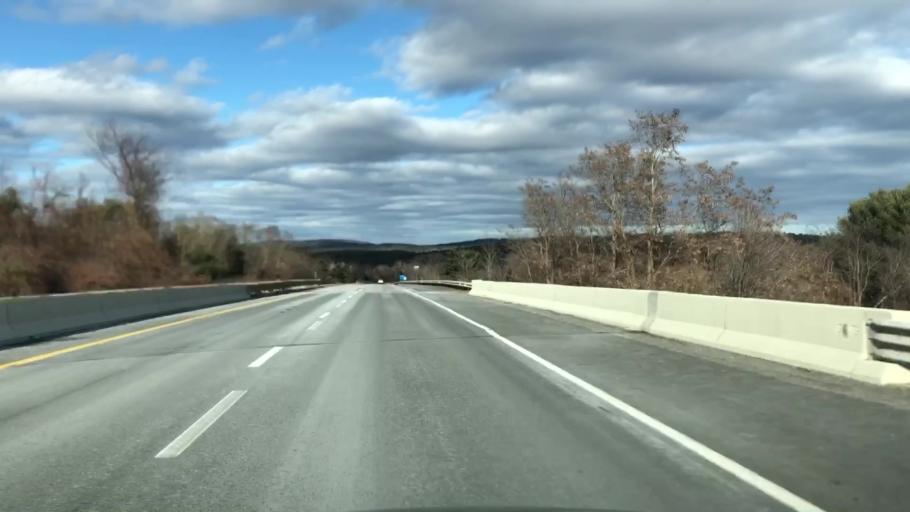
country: US
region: Massachusetts
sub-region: Worcester County
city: West Boylston
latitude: 42.4091
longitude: -71.7947
